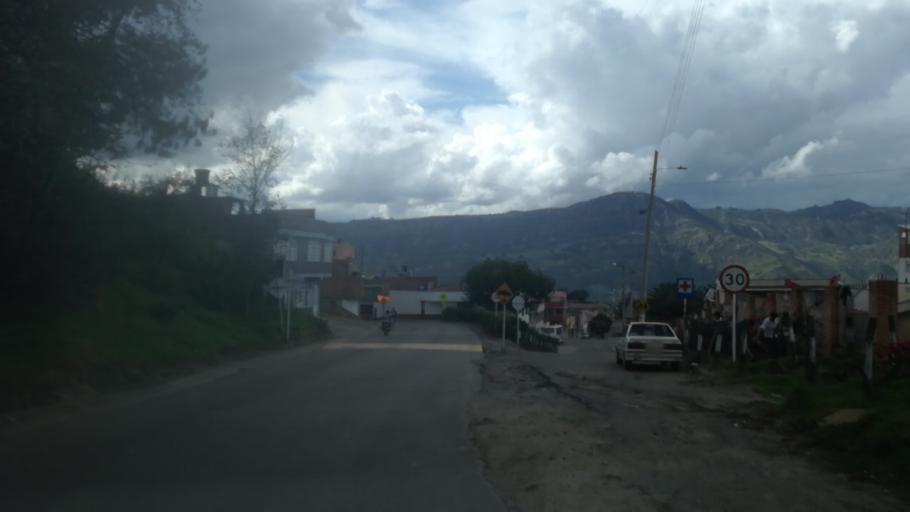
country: CO
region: Boyaca
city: Socha Viejo
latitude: 5.9960
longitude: -72.6892
